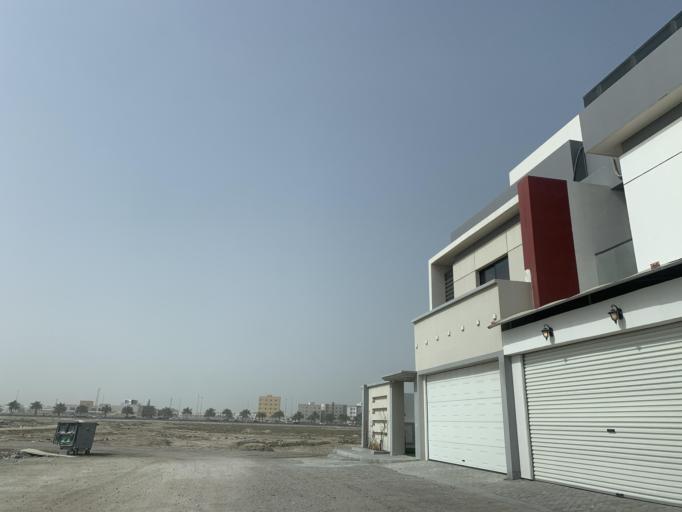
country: BH
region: Northern
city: Madinat `Isa
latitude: 26.1882
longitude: 50.5150
